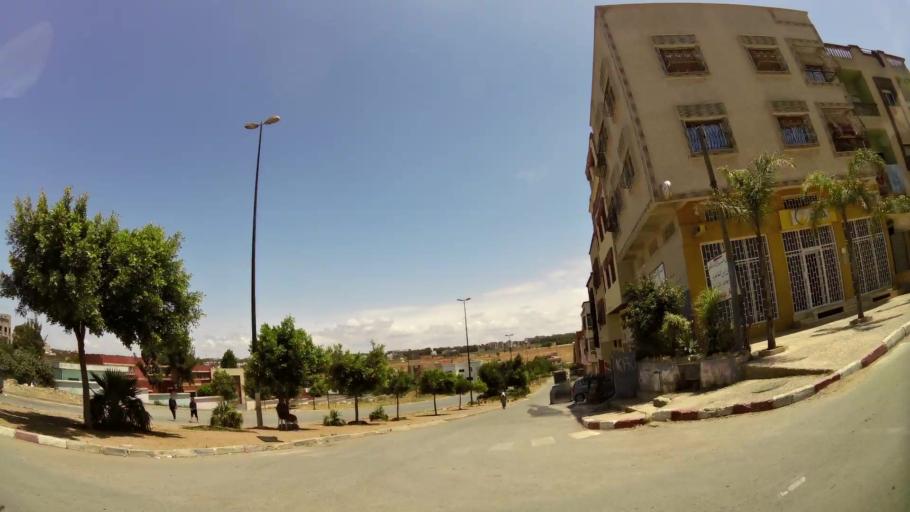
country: MA
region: Gharb-Chrarda-Beni Hssen
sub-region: Kenitra Province
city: Kenitra
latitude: 34.2639
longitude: -6.6435
